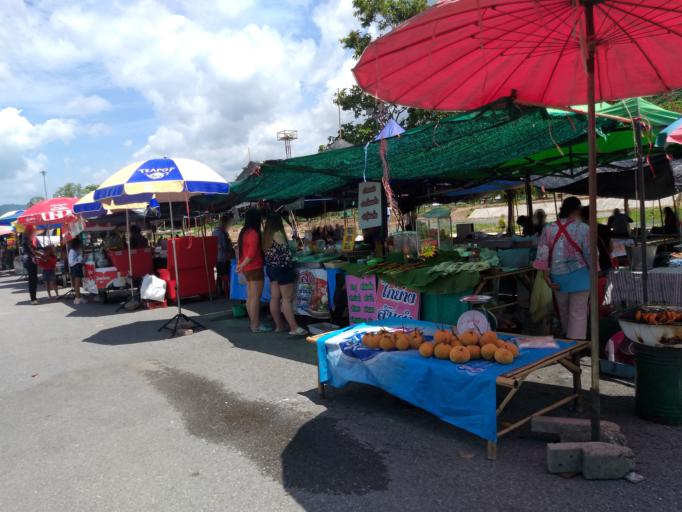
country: TH
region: Nakhon Nayok
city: Nakhon Nayok
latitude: 14.3110
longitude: 101.3192
